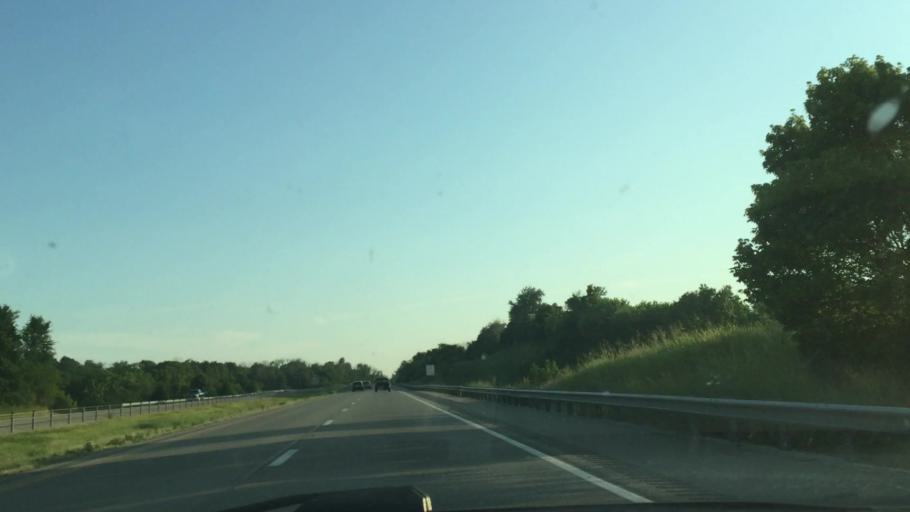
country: US
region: Kentucky
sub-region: Boone County
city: Verona
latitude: 38.8204
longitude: -84.7010
